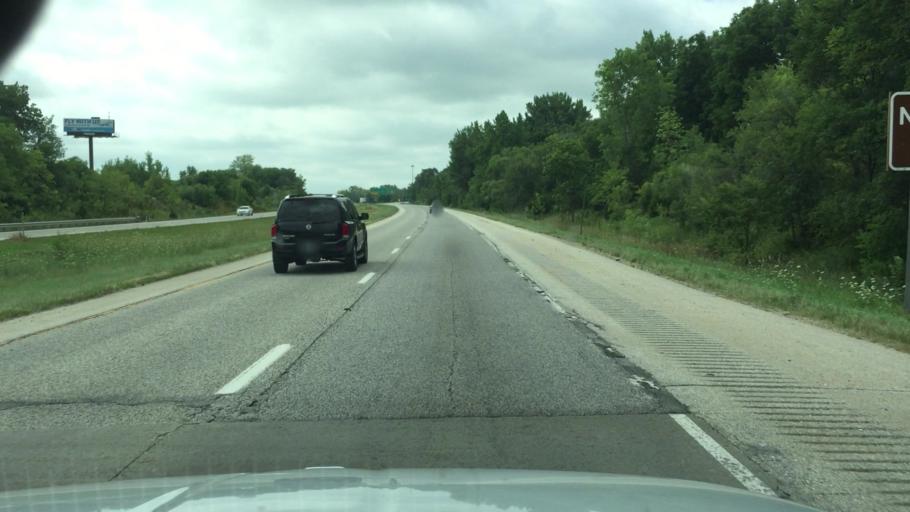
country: US
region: Illinois
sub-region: Henry County
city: Green Rock
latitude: 41.4631
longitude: -90.3389
